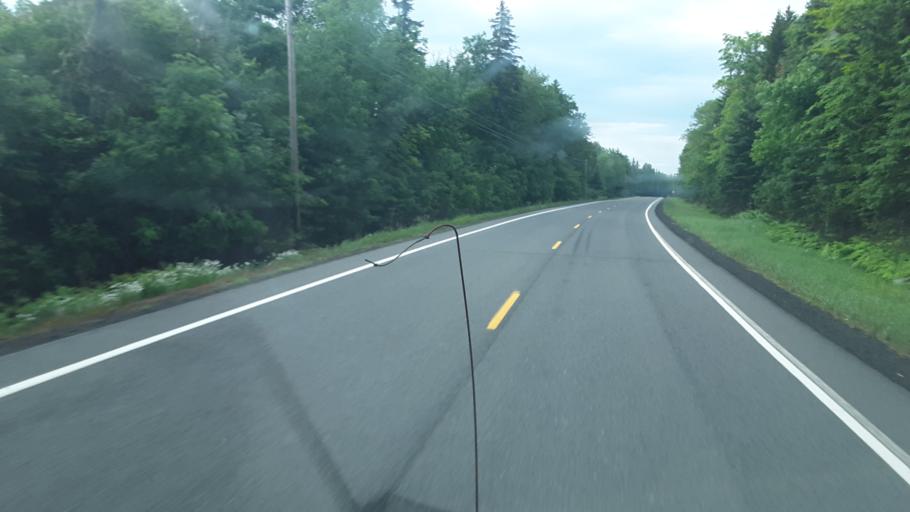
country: US
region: Maine
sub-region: Penobscot County
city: Patten
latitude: 46.2826
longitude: -68.3539
